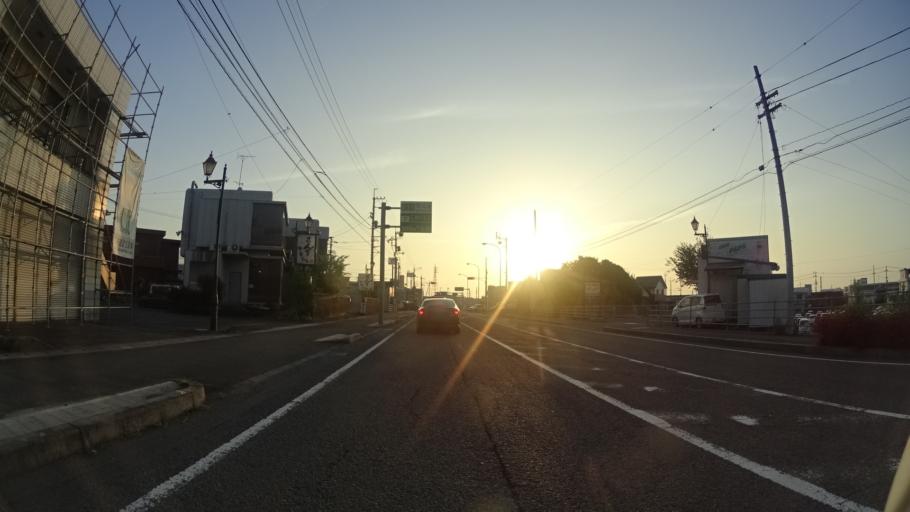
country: JP
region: Ehime
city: Kawanoecho
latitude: 33.9909
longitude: 133.5847
